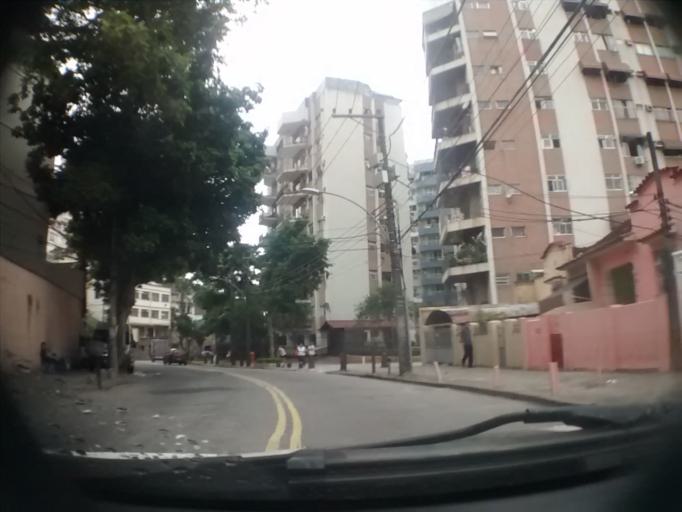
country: BR
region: Rio de Janeiro
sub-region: Rio De Janeiro
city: Rio de Janeiro
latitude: -22.9393
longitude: -43.2514
